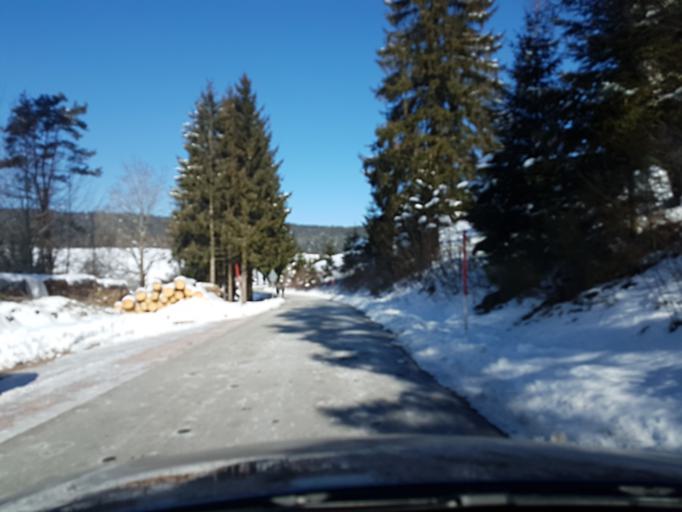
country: DE
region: Baden-Wuerttemberg
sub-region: Freiburg Region
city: Sankt Georgen im Schwarzwald
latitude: 48.1555
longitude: 8.2960
